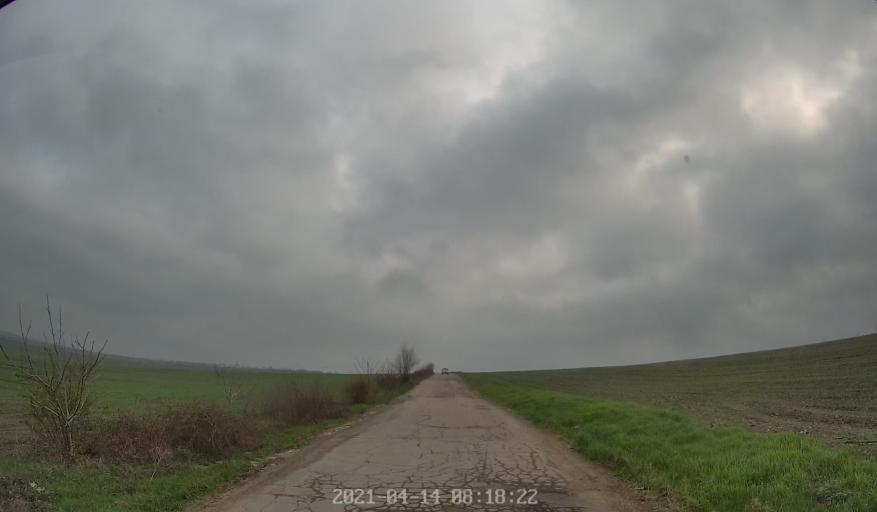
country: MD
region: Chisinau
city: Stauceni
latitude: 47.0554
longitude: 28.9171
